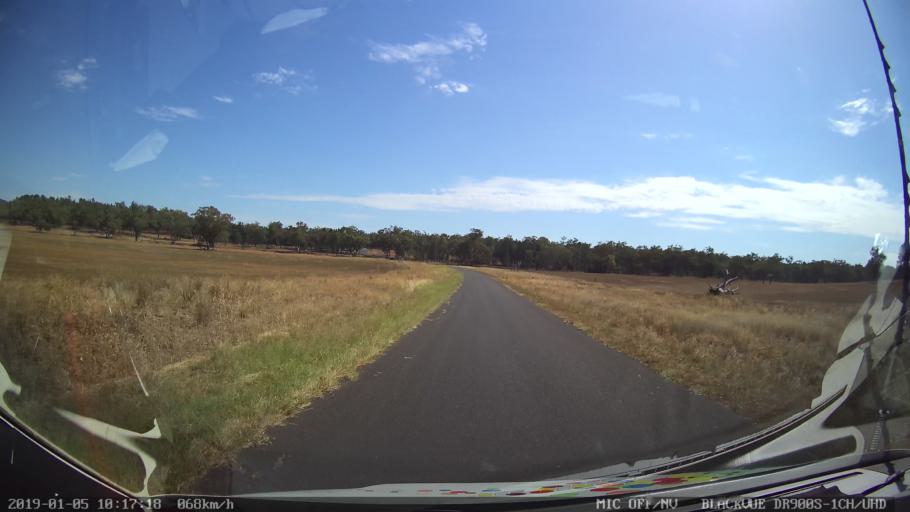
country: AU
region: New South Wales
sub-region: Gilgandra
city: Gilgandra
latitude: -31.5683
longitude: 148.9596
